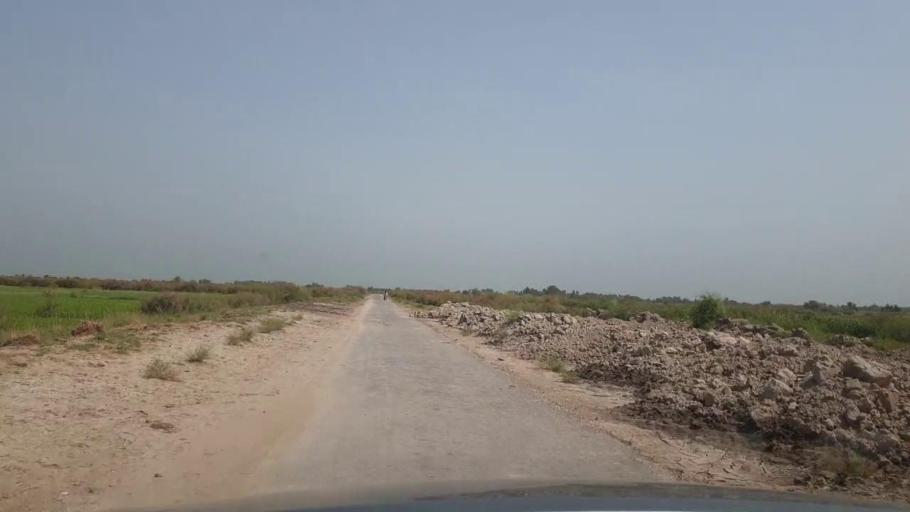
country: PK
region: Sindh
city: Madeji
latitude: 27.8290
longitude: 68.4470
